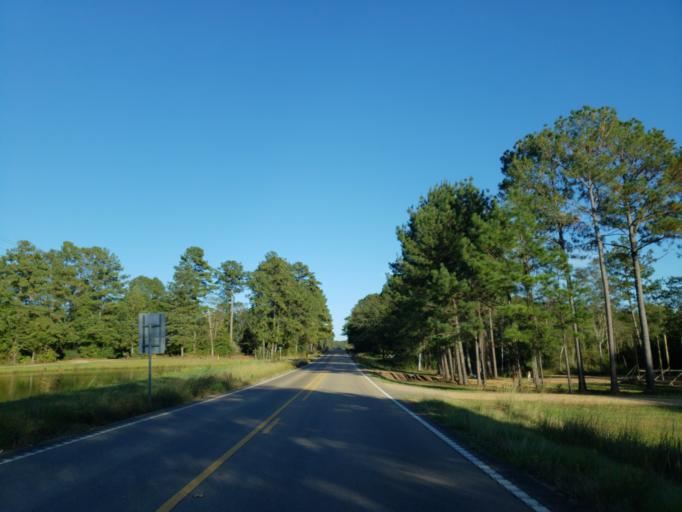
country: US
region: Mississippi
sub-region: Perry County
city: Richton
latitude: 31.3760
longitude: -88.8555
